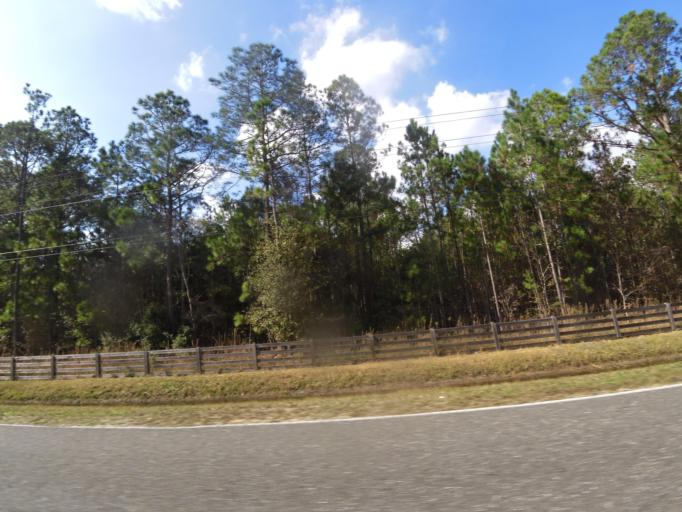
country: US
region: Florida
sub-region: Duval County
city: Baldwin
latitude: 30.1561
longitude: -82.0016
